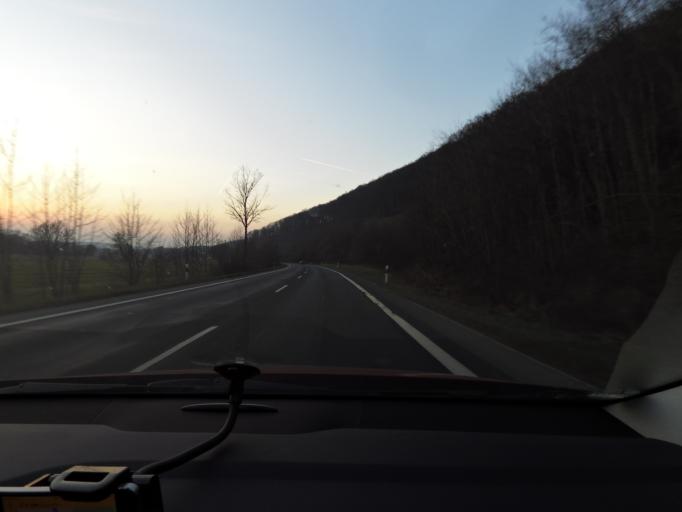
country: DE
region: Hesse
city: Witzenhausen
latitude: 51.3878
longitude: 9.7969
